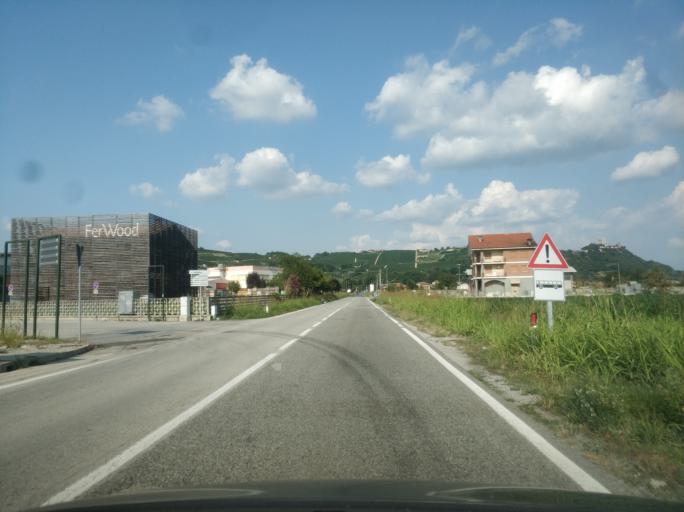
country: IT
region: Piedmont
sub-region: Provincia di Cuneo
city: Cinzano
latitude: 44.6909
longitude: 7.9044
